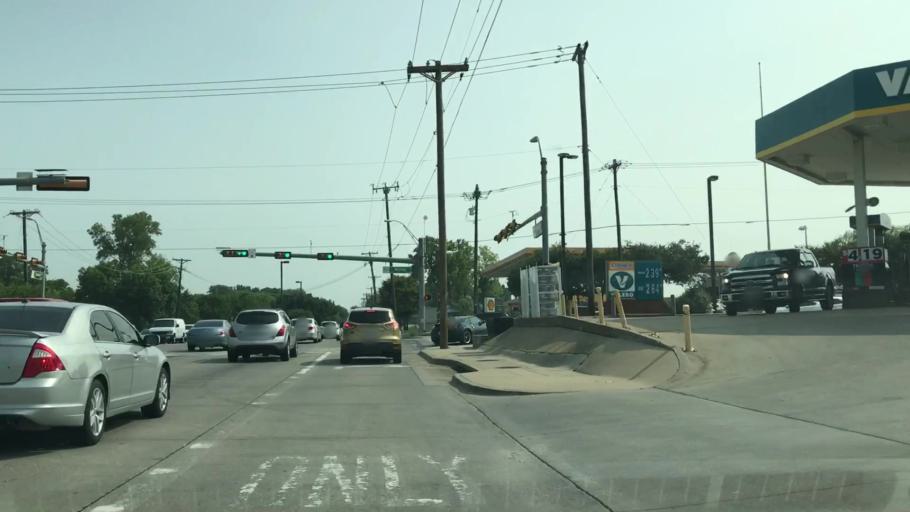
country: US
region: Texas
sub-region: Dallas County
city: Rowlett
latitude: 32.8943
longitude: -96.5696
